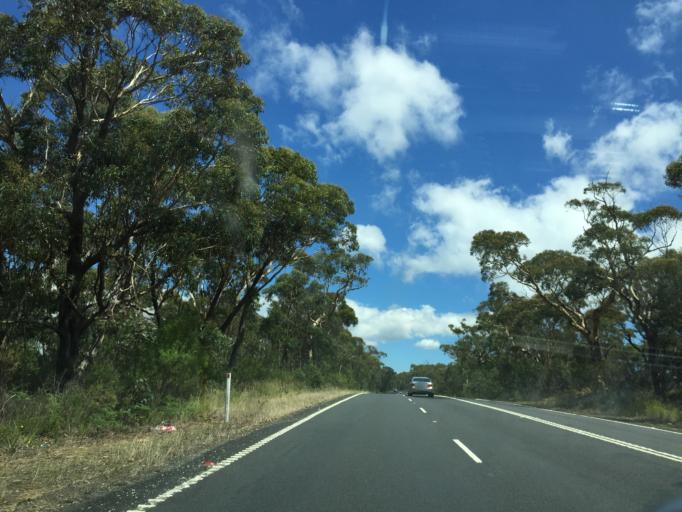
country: AU
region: New South Wales
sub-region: Blue Mountains Municipality
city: Blackheath
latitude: -33.5679
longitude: 150.3626
